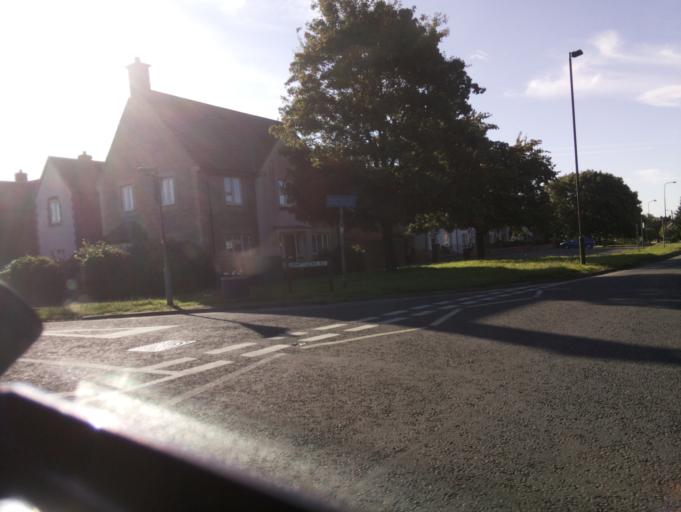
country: GB
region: England
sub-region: South Gloucestershire
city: Kingswood
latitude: 51.4397
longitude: -2.5194
